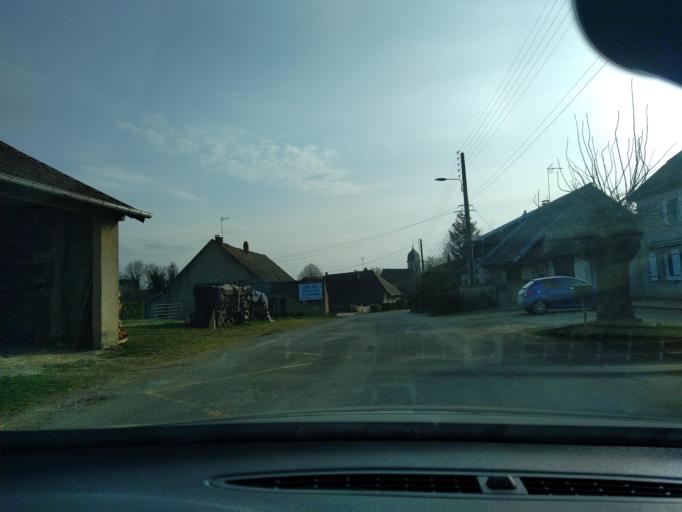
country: FR
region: Franche-Comte
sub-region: Departement du Jura
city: Chaussin
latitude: 46.9896
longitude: 5.4640
